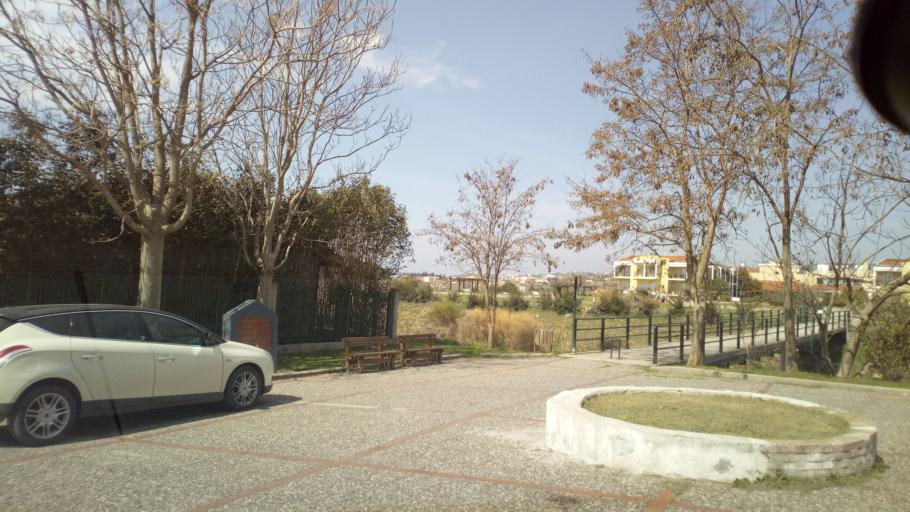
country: GR
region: Central Macedonia
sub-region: Nomos Thessalonikis
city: Thermi
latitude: 40.5450
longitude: 23.0340
